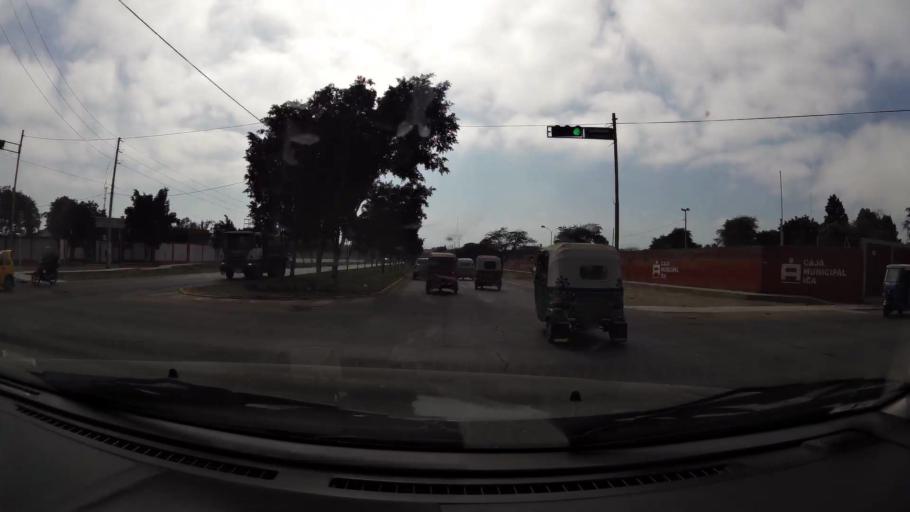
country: PE
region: Ica
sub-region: Provincia de Ica
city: Ica
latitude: -14.0754
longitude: -75.7340
